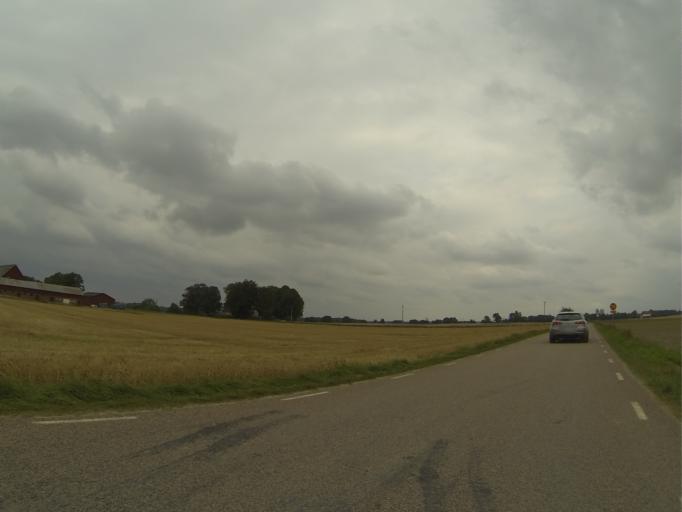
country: SE
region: Skane
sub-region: Lunds Kommun
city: Lund
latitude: 55.7792
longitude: 13.2015
